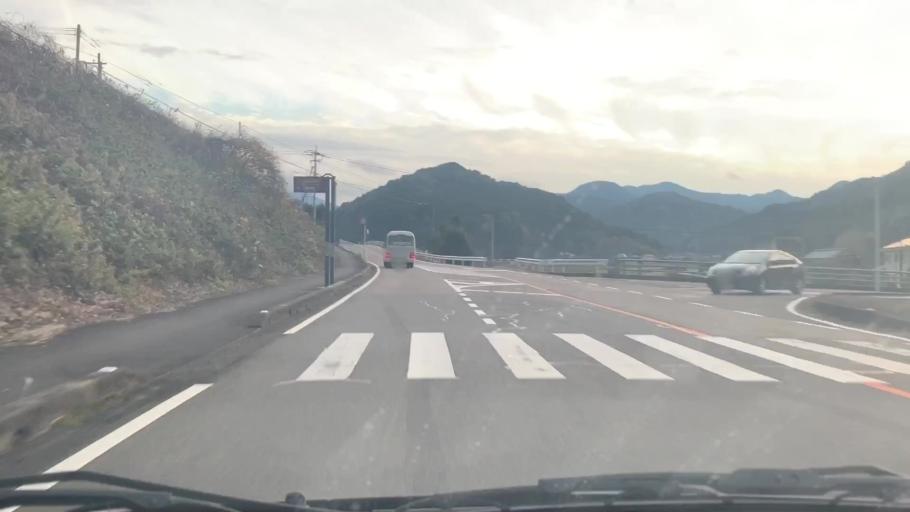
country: JP
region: Saga Prefecture
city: Kashima
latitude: 33.0777
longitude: 130.0673
